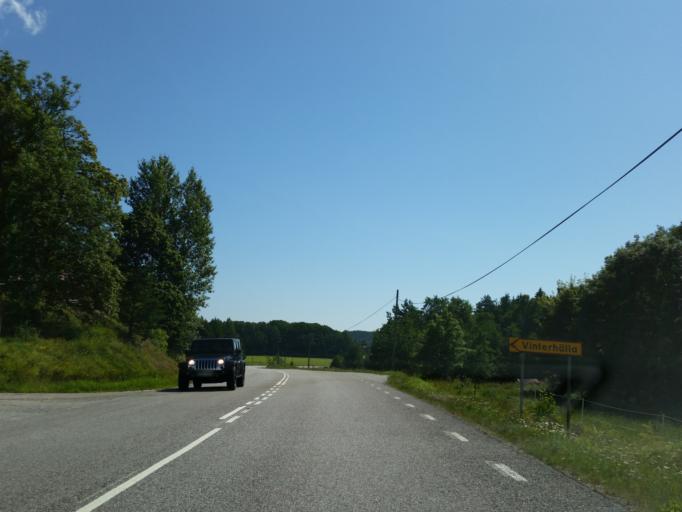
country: SE
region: Soedermanland
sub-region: Trosa Kommun
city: Vagnharad
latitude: 58.9958
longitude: 17.6117
